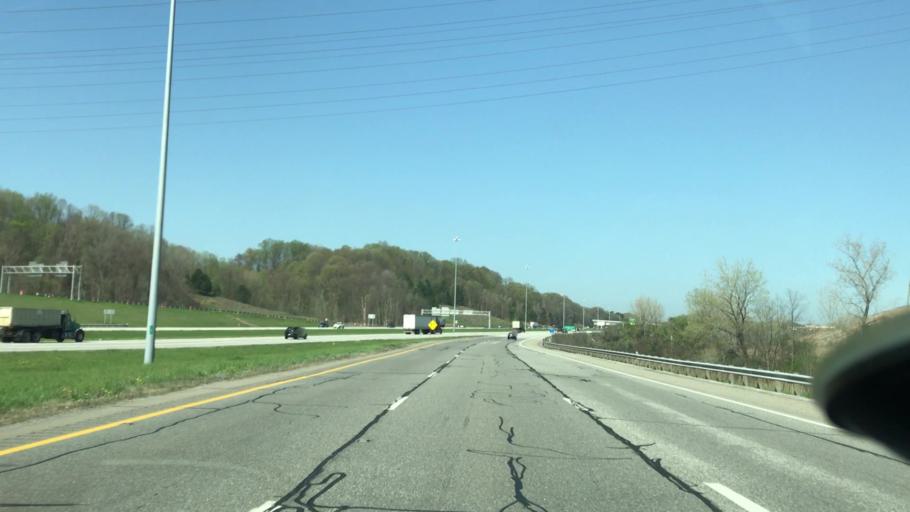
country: US
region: Ohio
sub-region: Cuyahoga County
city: Seven Hills
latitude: 41.4086
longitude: -81.6503
